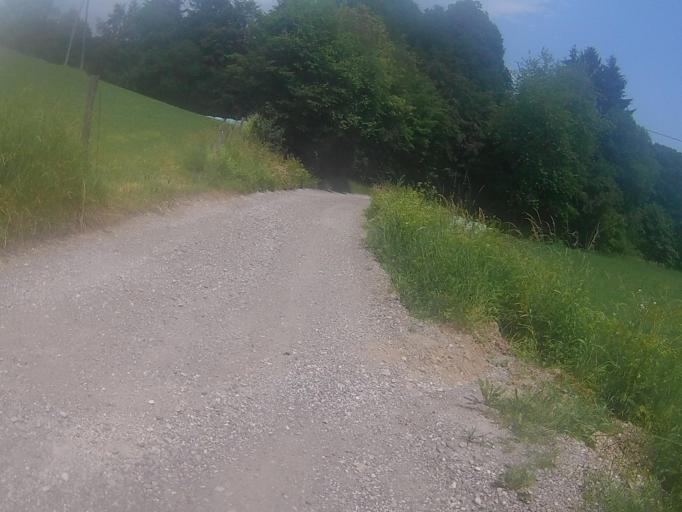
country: SI
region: Maribor
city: Kamnica
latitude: 46.5990
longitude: 15.5915
